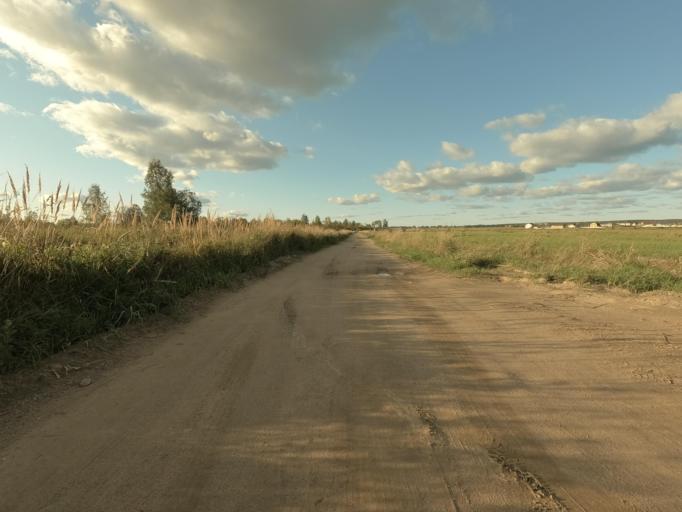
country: RU
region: Leningrad
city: Imeni Sverdlova
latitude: 59.8633
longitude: 30.7305
